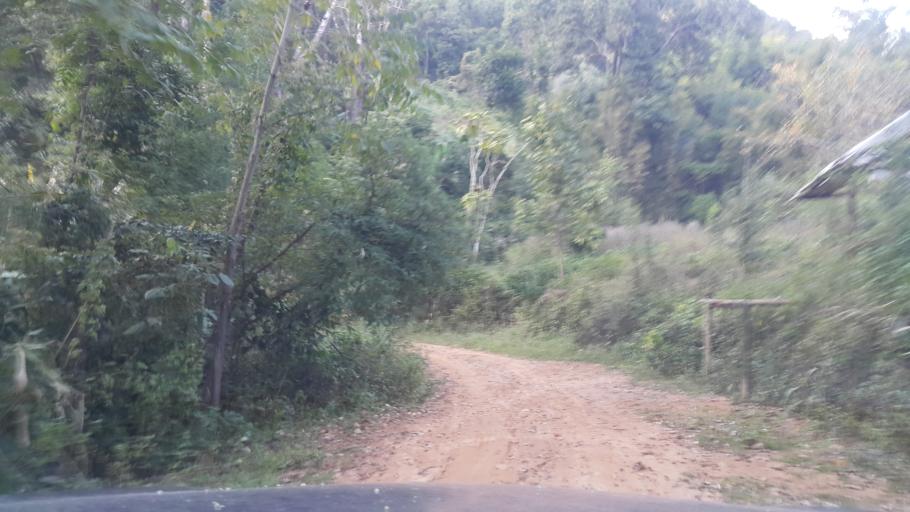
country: TH
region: Chiang Mai
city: Samoeng
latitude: 19.0091
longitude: 98.6481
